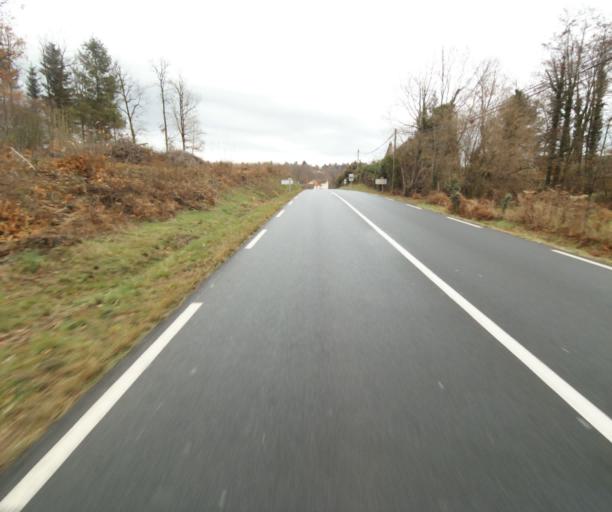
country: FR
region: Limousin
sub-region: Departement de la Correze
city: Saint-Mexant
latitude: 45.2762
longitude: 1.6293
